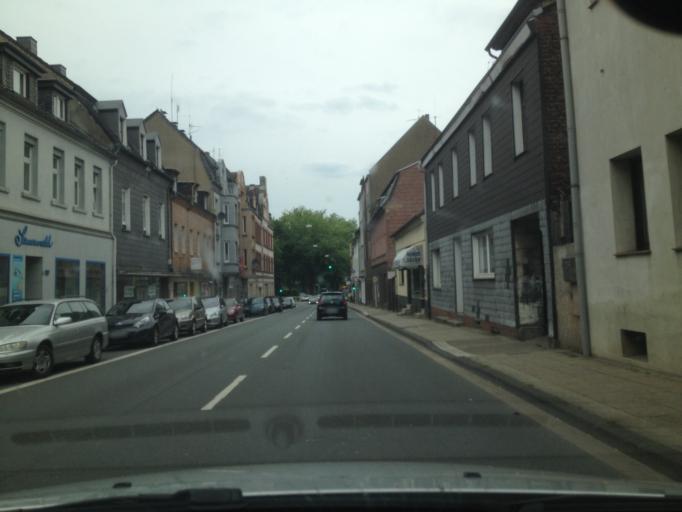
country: DE
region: North Rhine-Westphalia
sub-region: Regierungsbezirk Munster
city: Gelsenkirchen
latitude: 51.4604
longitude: 7.0783
